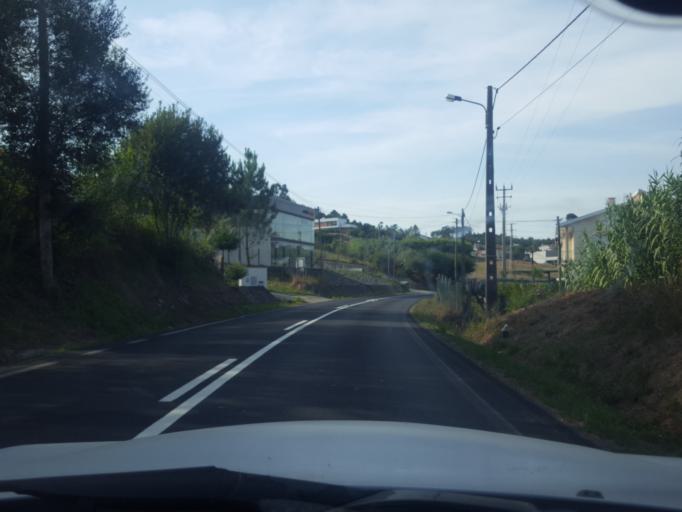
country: PT
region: Leiria
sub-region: Leiria
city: Leiria
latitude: 39.7028
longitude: -8.7919
